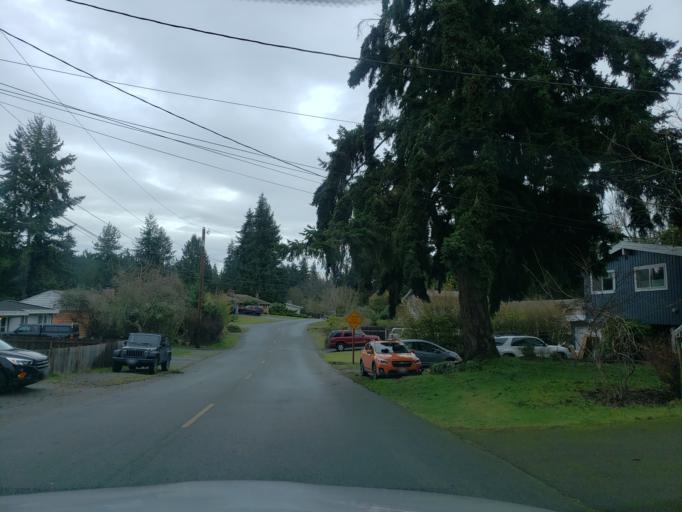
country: US
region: Washington
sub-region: Snohomish County
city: Lynnwood
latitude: 47.8257
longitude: -122.3404
